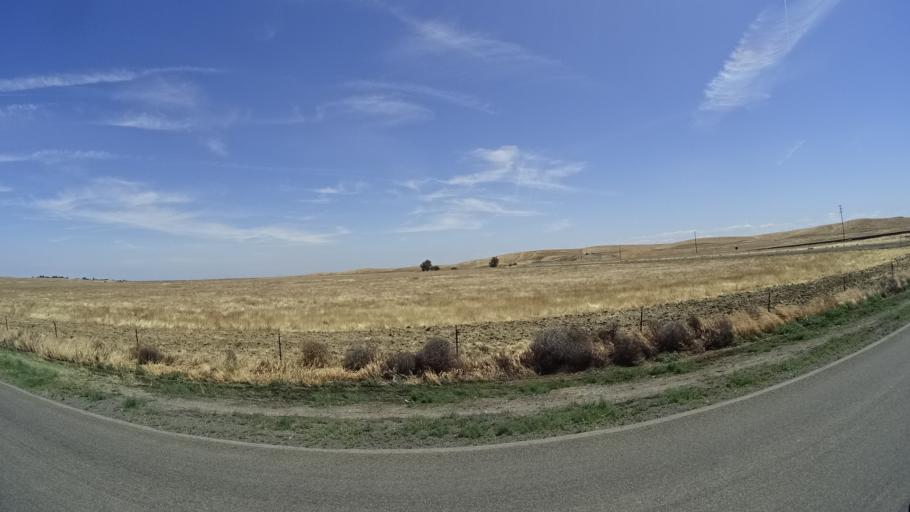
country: US
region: California
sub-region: Kings County
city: Kettleman City
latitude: 35.8447
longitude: -119.9153
